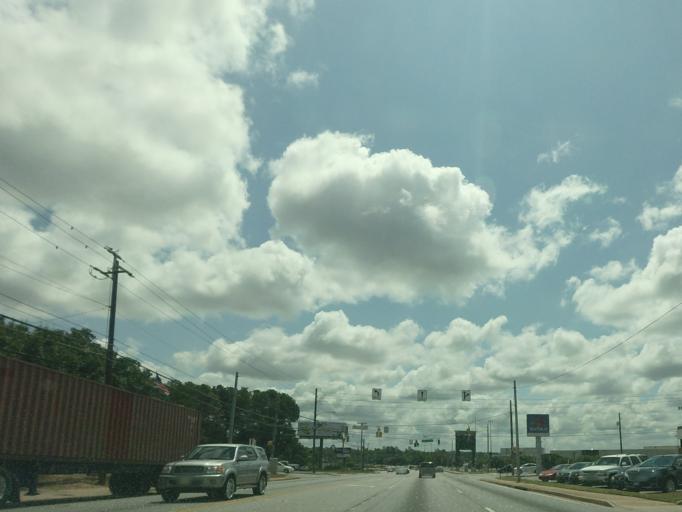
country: US
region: Georgia
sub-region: Bibb County
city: Macon
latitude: 32.8213
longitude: -83.6964
